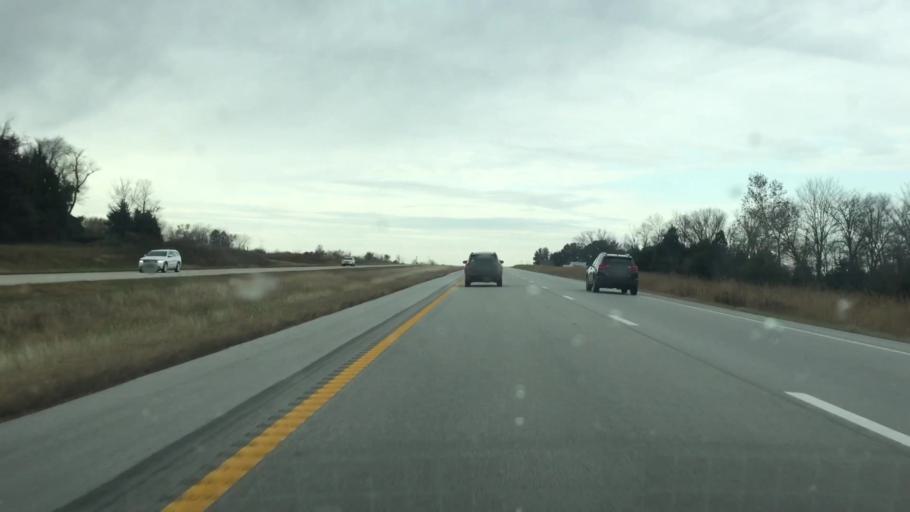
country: US
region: Missouri
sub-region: Saint Clair County
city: Osceola
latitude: 38.1791
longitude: -93.7256
